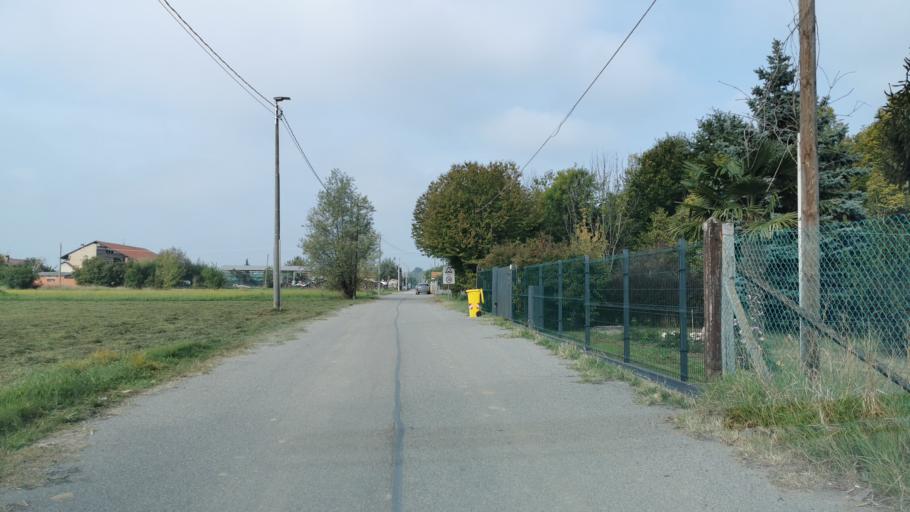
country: IT
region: Piedmont
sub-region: Provincia di Torino
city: Front
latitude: 45.2586
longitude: 7.6615
